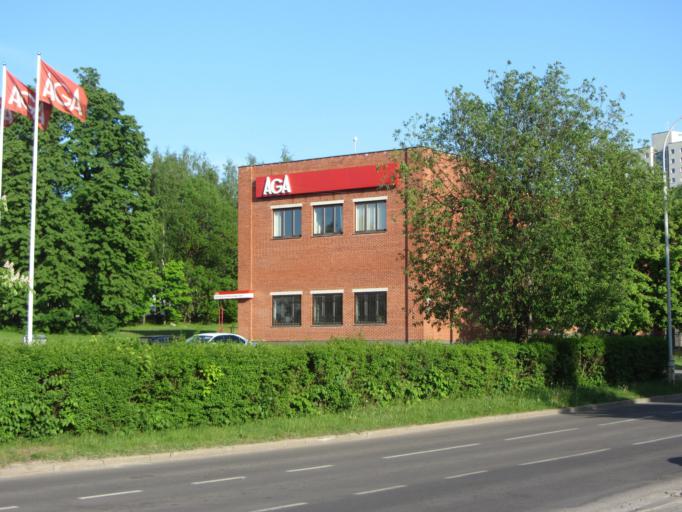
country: LT
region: Vilnius County
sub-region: Vilnius
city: Fabijoniskes
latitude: 54.7349
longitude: 25.2590
